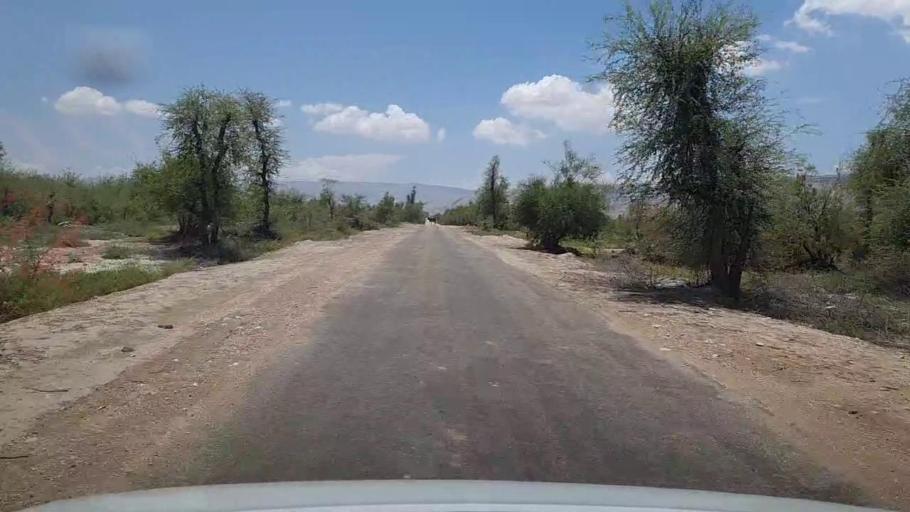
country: PK
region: Sindh
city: Bhan
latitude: 26.2801
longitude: 67.5290
